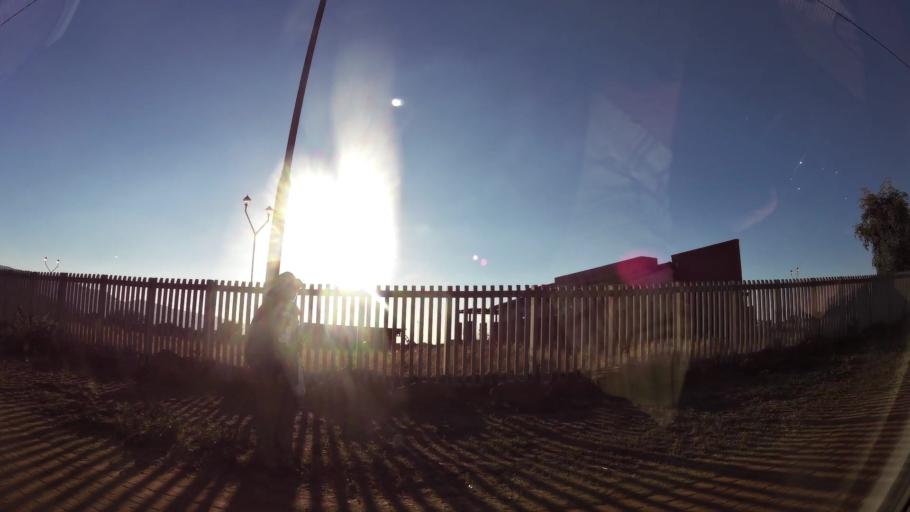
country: ZA
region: Limpopo
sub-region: Waterberg District Municipality
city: Mokopane
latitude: -24.1449
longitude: 28.9898
